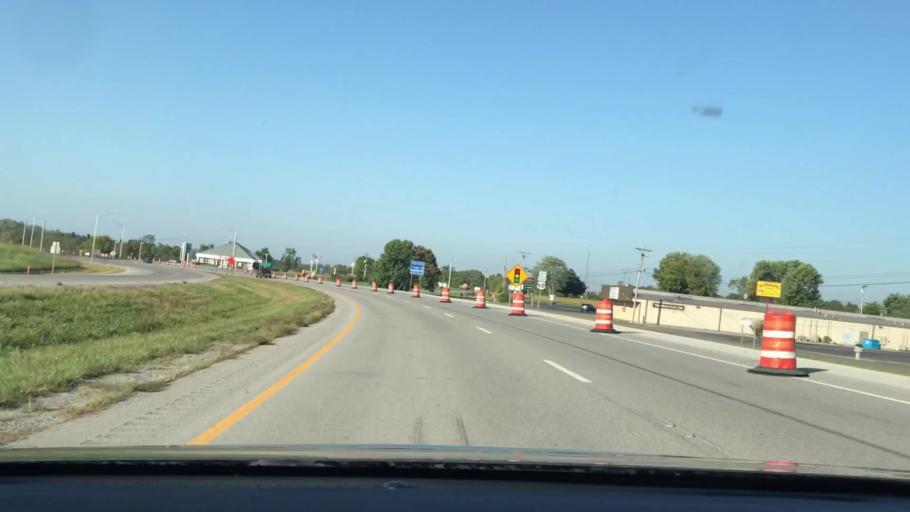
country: US
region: Kentucky
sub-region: Trigg County
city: Cadiz
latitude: 36.8676
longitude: -87.7936
